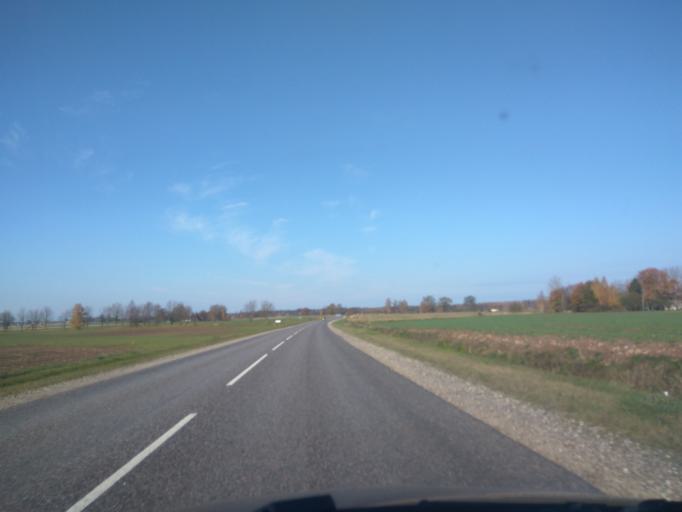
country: LV
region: Kuldigas Rajons
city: Kuldiga
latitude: 57.0004
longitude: 21.8977
